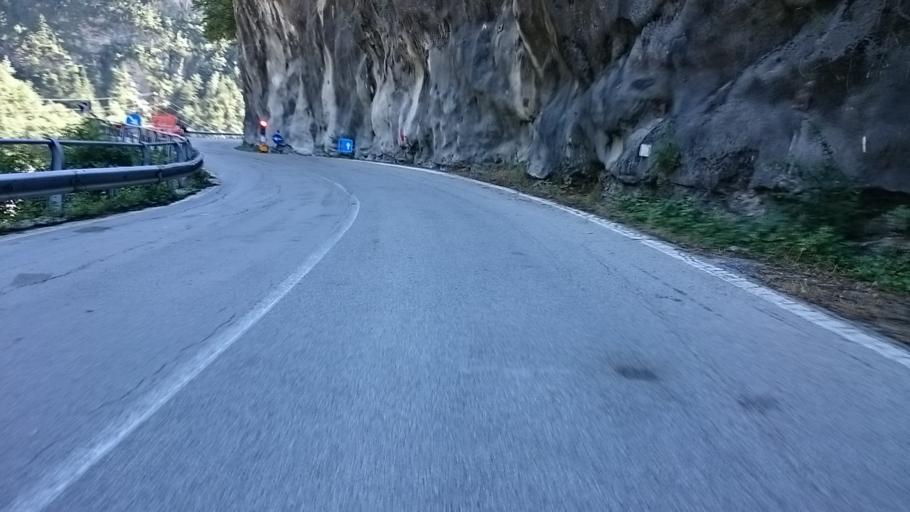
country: IT
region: Veneto
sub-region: Provincia di Belluno
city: Ospitale di Cadore
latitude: 46.3348
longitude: 12.3309
